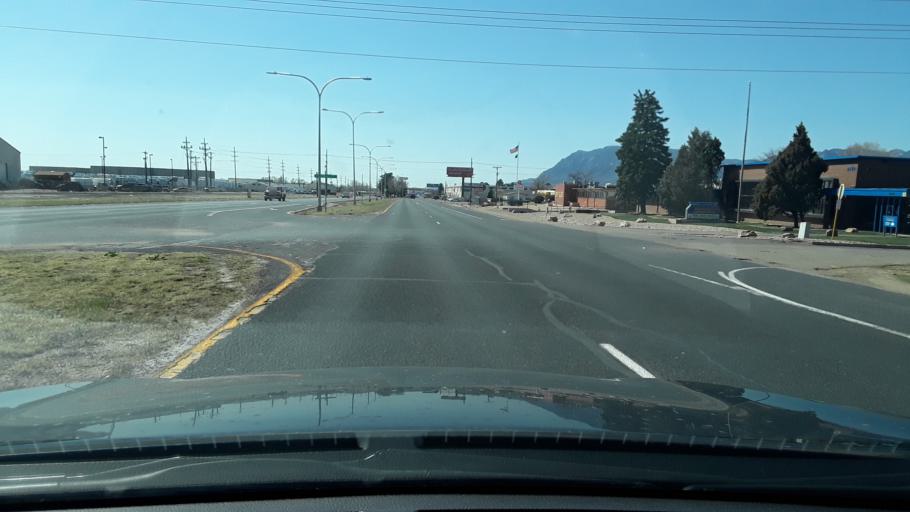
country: US
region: Colorado
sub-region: El Paso County
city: Colorado Springs
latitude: 38.8817
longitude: -104.8189
